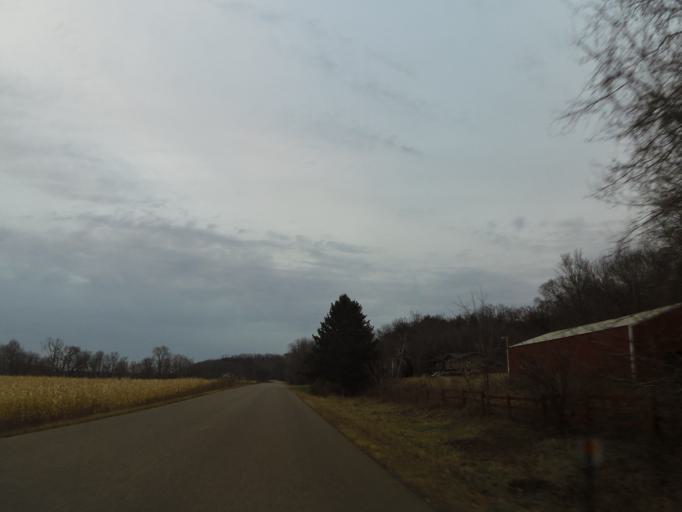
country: US
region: Wisconsin
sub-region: Pierce County
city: River Falls
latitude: 44.8790
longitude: -92.6086
